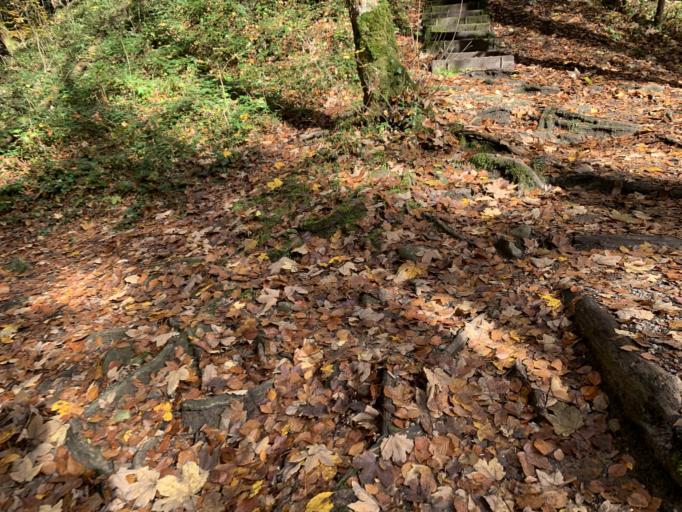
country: CH
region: Zurich
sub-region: Bezirk Hinwil
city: Hinwil
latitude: 47.3091
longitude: 8.8539
